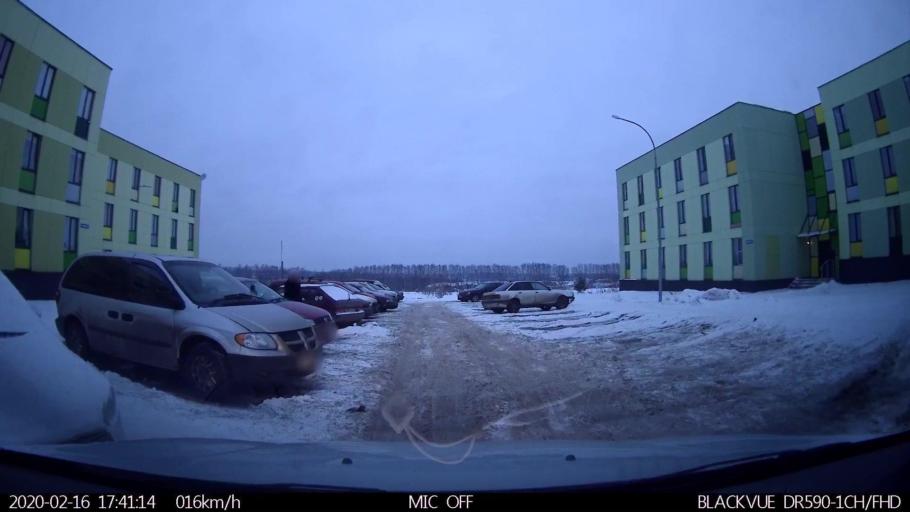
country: RU
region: Nizjnij Novgorod
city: Afonino
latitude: 56.2159
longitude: 44.0216
